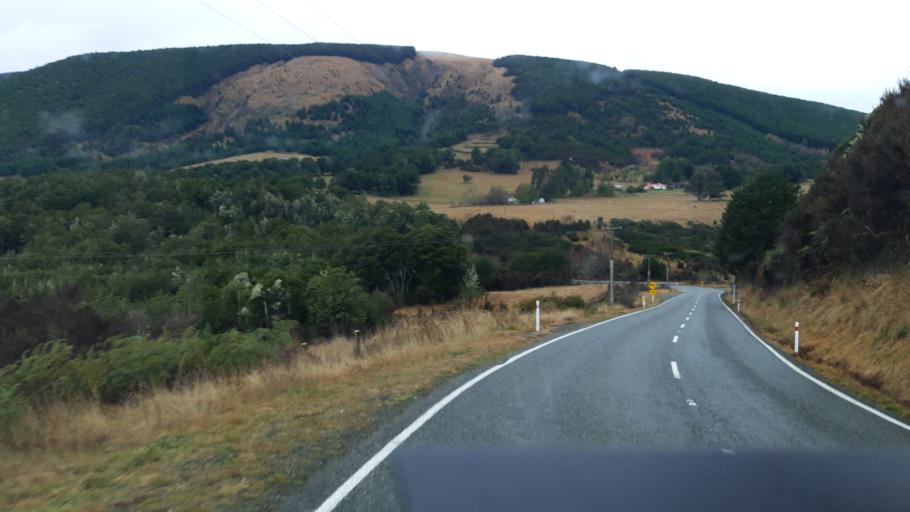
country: NZ
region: Tasman
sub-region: Tasman District
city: Wakefield
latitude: -41.7639
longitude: 172.8931
